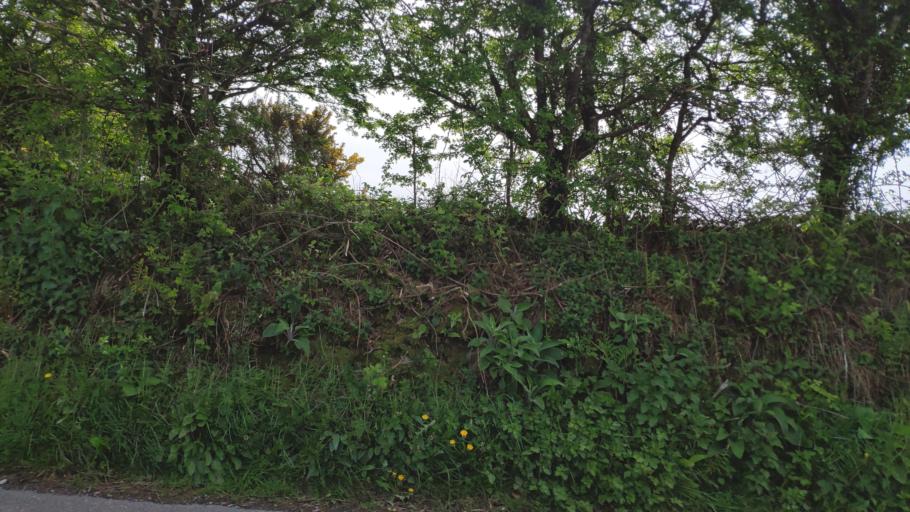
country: IE
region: Munster
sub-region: County Cork
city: Blarney
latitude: 51.9856
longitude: -8.5102
